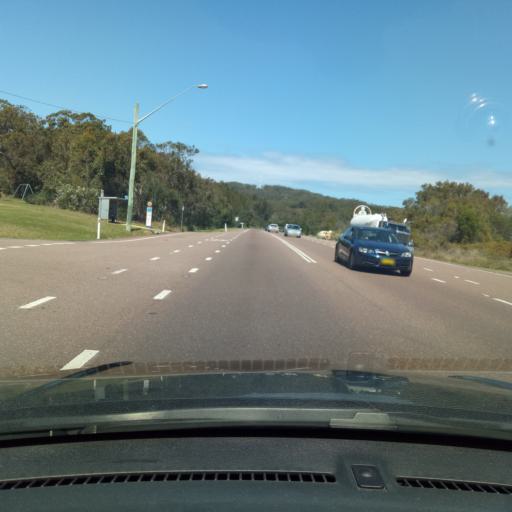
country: AU
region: New South Wales
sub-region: Wyong Shire
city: Bateau Bay
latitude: -33.3932
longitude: 151.4738
